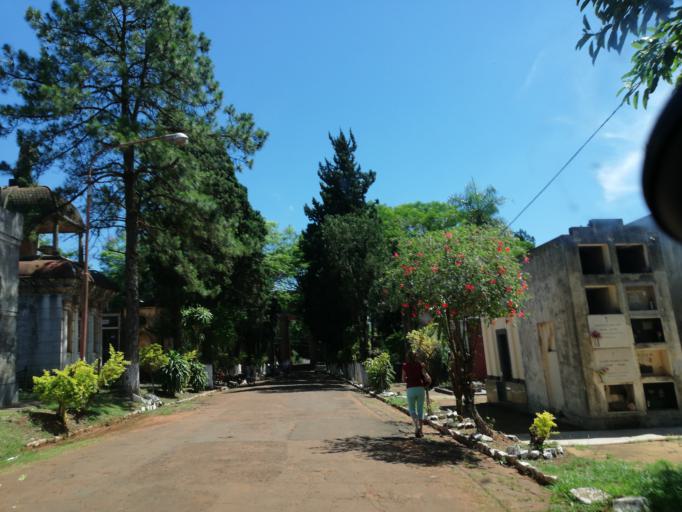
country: AR
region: Misiones
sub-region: Departamento de Capital
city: Posadas
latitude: -27.3806
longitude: -55.9127
